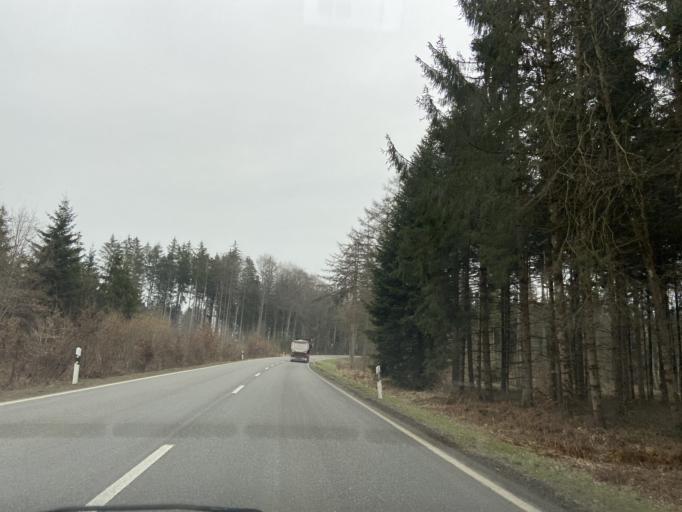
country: DE
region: Baden-Wuerttemberg
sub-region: Tuebingen Region
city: Ennetach
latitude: 47.9952
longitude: 9.3069
